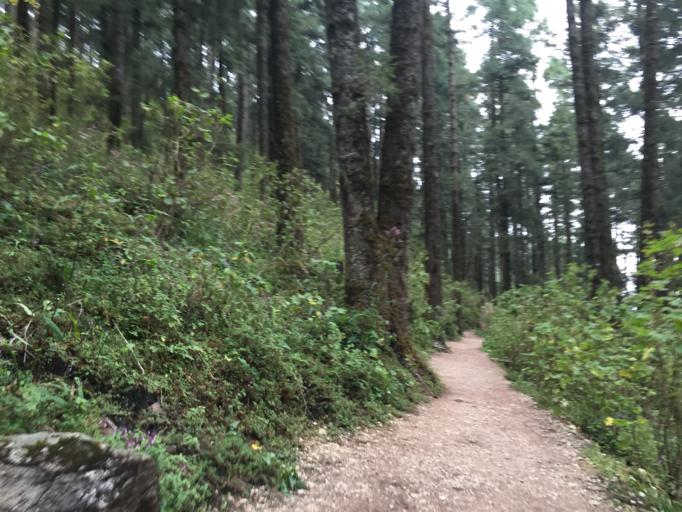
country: MX
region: Michoacan
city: Mineral de Angangueo
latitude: 19.6725
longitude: -100.2905
